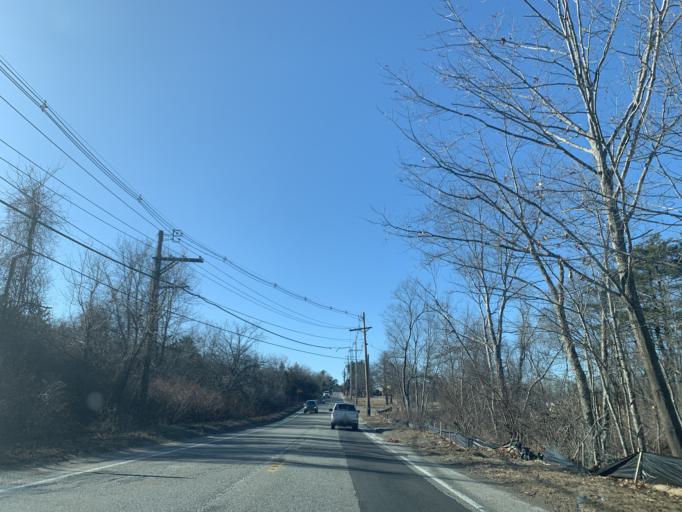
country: US
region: Massachusetts
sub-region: Middlesex County
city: Wayland
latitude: 42.3631
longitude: -71.3797
